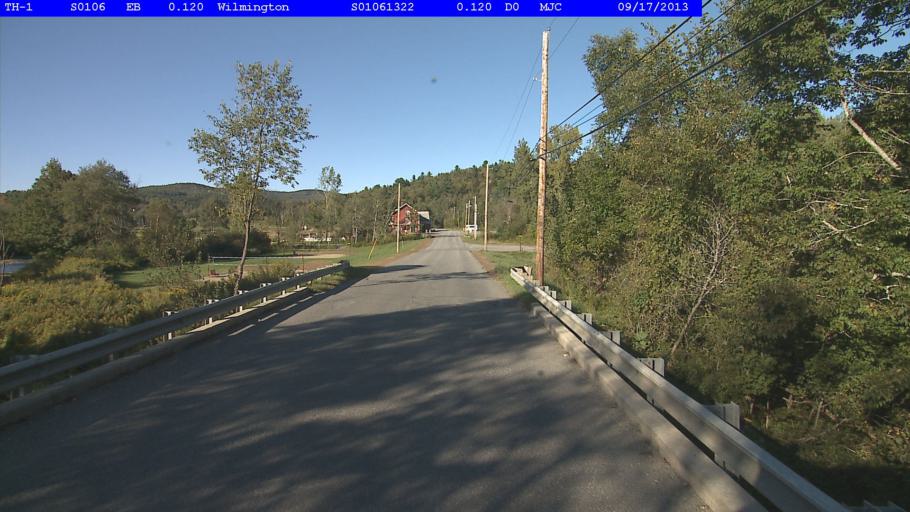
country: US
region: Vermont
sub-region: Windham County
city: Dover
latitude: 42.9144
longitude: -72.8376
